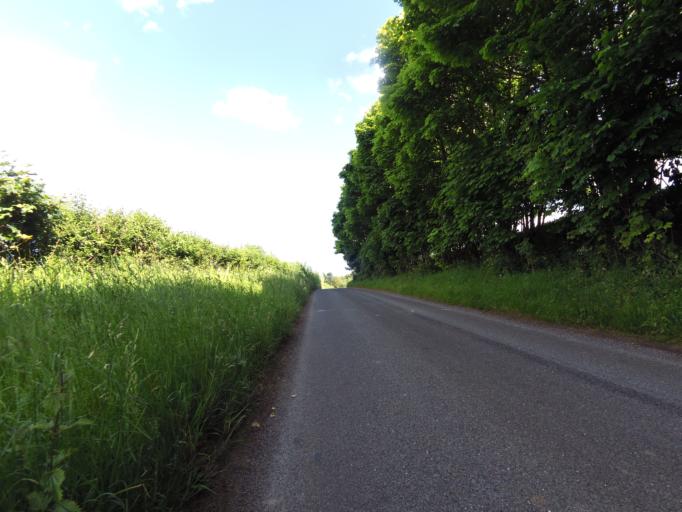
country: GB
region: England
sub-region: Suffolk
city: Shotley Gate
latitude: 52.0076
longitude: 1.2461
